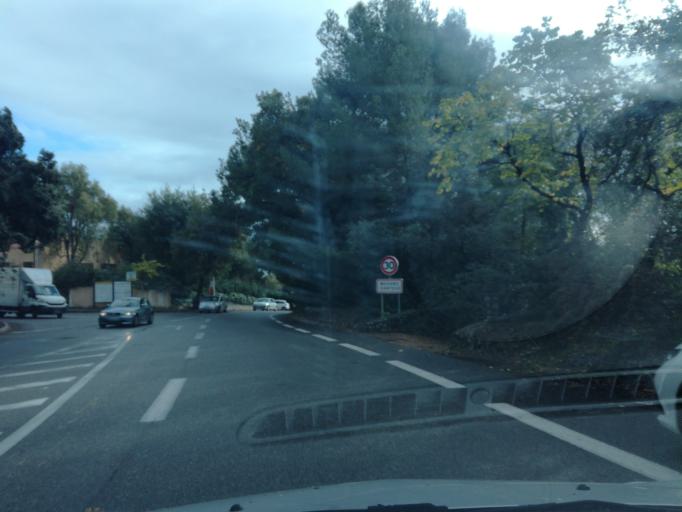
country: FR
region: Provence-Alpes-Cote d'Azur
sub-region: Departement des Alpes-Maritimes
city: Pegomas
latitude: 43.6230
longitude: 6.9351
